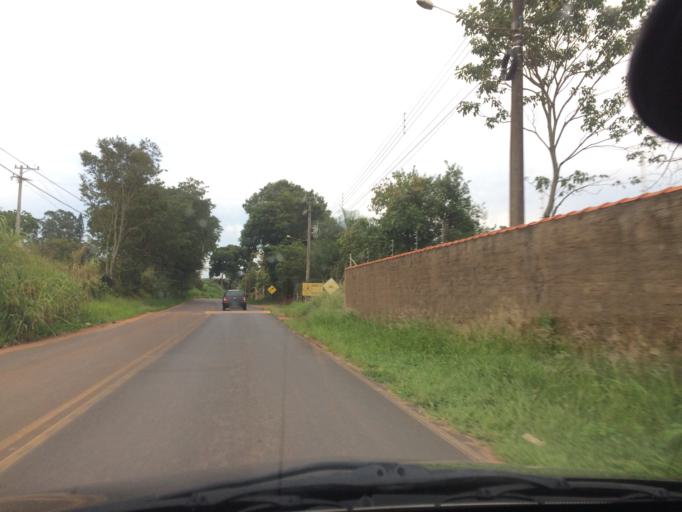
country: BR
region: Sao Paulo
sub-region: Casa Branca
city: Casa Branca
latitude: -21.7688
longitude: -47.0971
